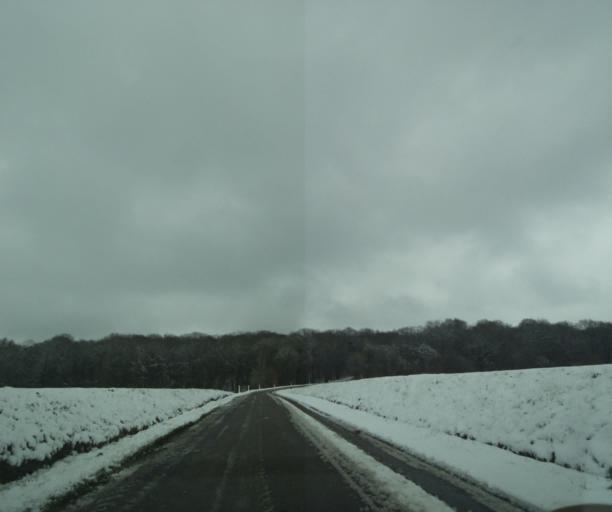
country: FR
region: Champagne-Ardenne
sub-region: Departement de la Haute-Marne
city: Laneuville-a-Remy
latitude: 48.3963
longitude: 4.8651
